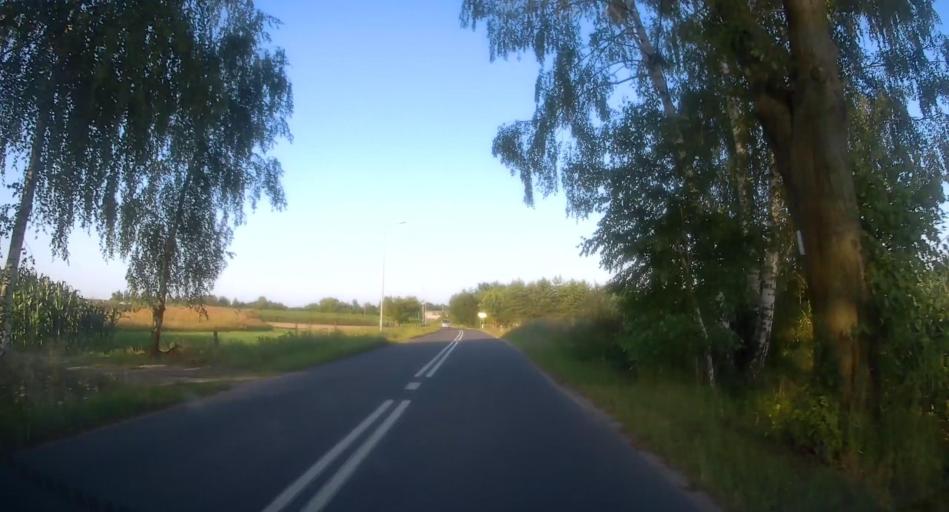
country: PL
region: Lodz Voivodeship
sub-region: Powiat skierniewicki
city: Kowiesy
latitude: 51.8882
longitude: 20.4045
